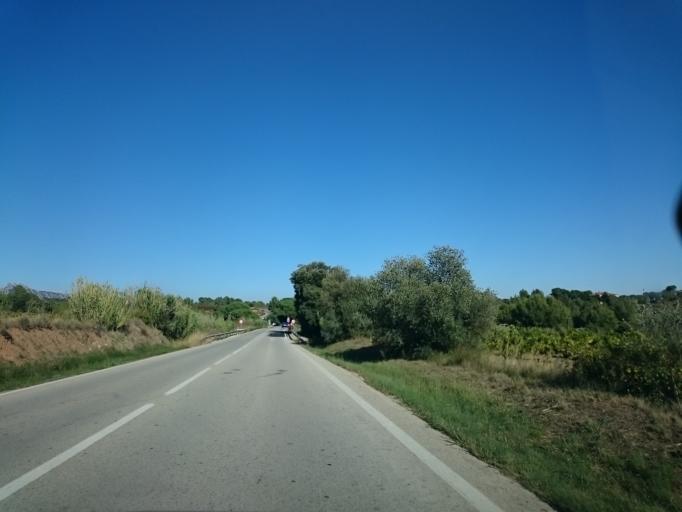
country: ES
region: Catalonia
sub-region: Provincia de Barcelona
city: Piera
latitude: 41.5321
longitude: 1.7231
